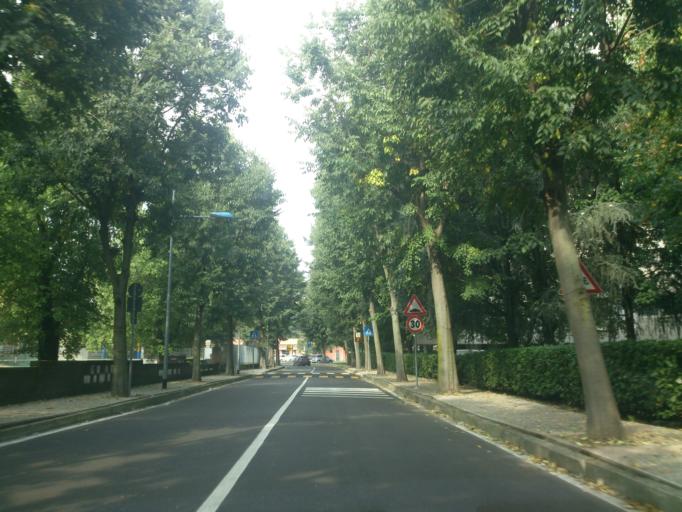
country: IT
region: Lombardy
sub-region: Citta metropolitana di Milano
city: San Donato Milanese
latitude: 45.4287
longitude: 9.2680
